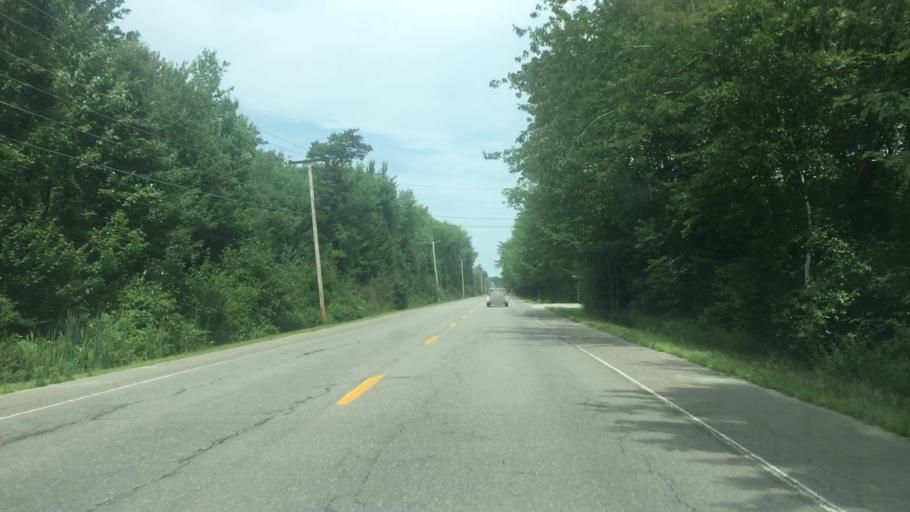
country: US
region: Maine
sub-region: Cumberland County
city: Scarborough
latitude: 43.5957
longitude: -70.2916
